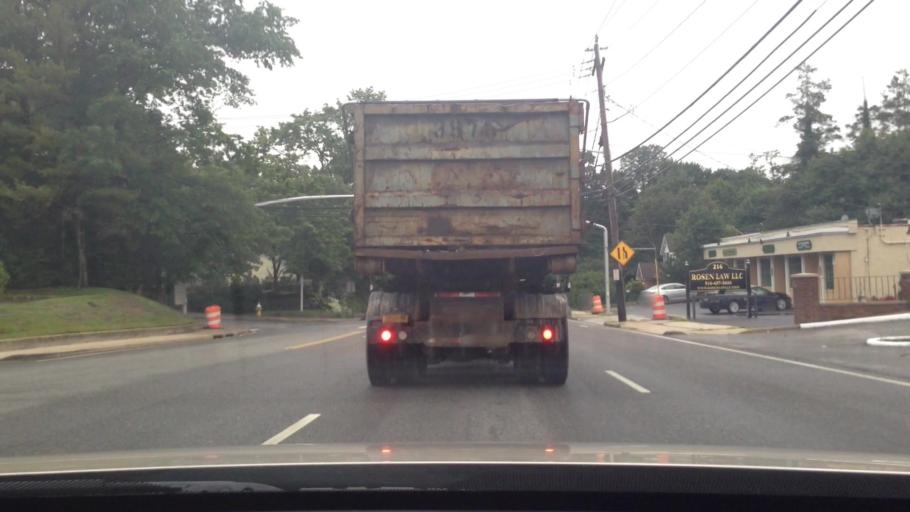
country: US
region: New York
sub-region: Nassau County
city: Thomaston
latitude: 40.7808
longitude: -73.7161
